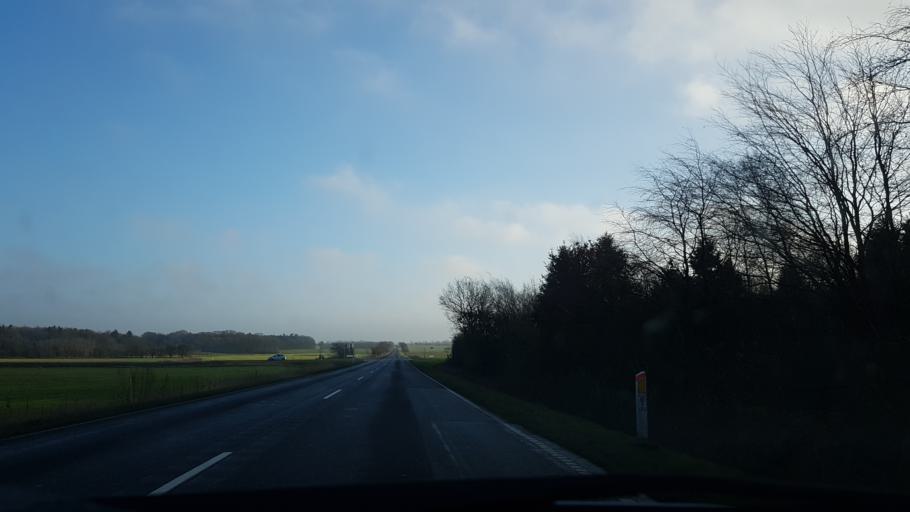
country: DK
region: South Denmark
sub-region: Haderslev Kommune
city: Vojens
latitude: 55.1770
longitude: 9.2430
